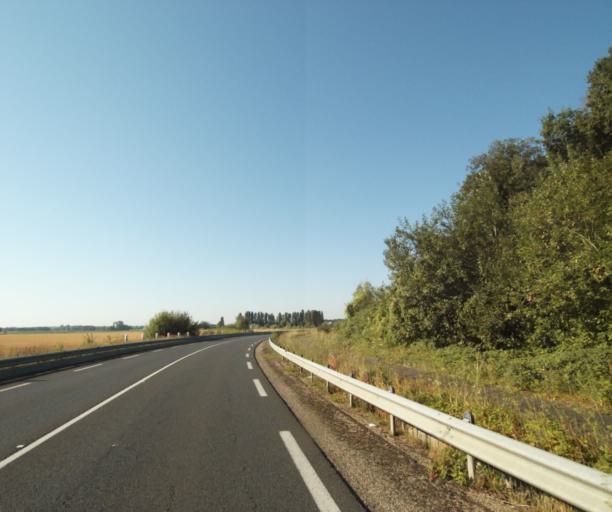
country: FR
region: Ile-de-France
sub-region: Departement de Seine-et-Marne
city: Vert-Saint-Denis
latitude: 48.5931
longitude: 2.6052
